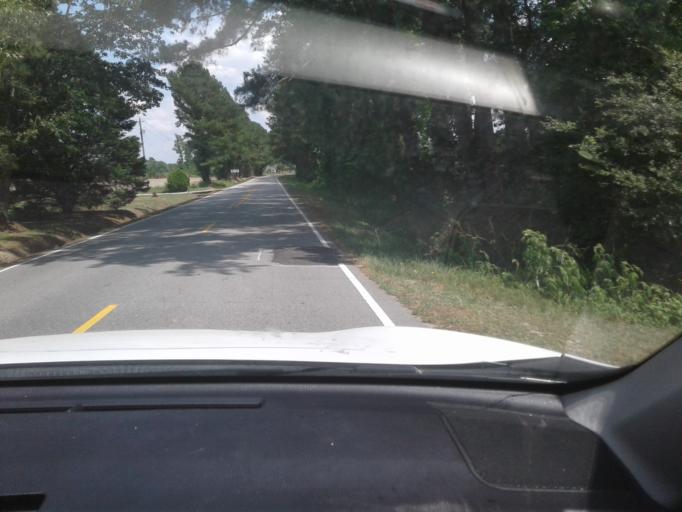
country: US
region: North Carolina
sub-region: Harnett County
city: Erwin
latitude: 35.2209
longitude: -78.6871
